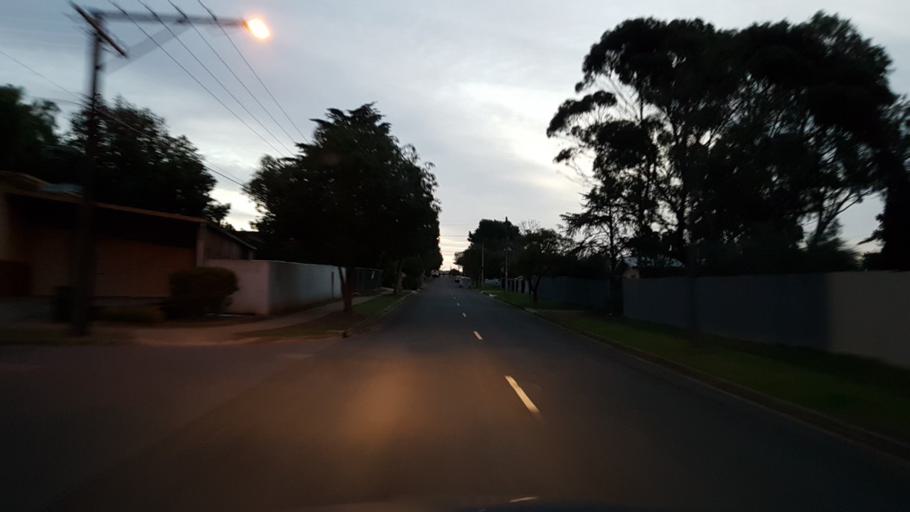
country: AU
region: South Australia
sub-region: Port Adelaide Enfield
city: Gilles Plains
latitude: -34.8463
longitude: 138.6631
